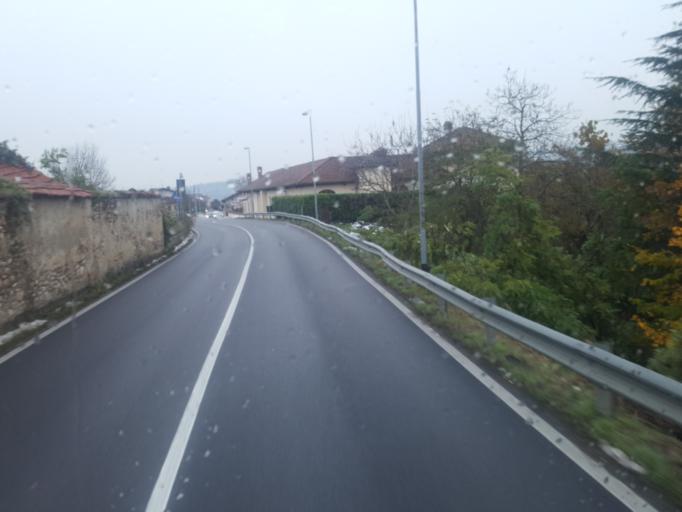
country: IT
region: Piedmont
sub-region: Provincia di Cuneo
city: Breo
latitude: 44.4058
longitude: 7.8330
